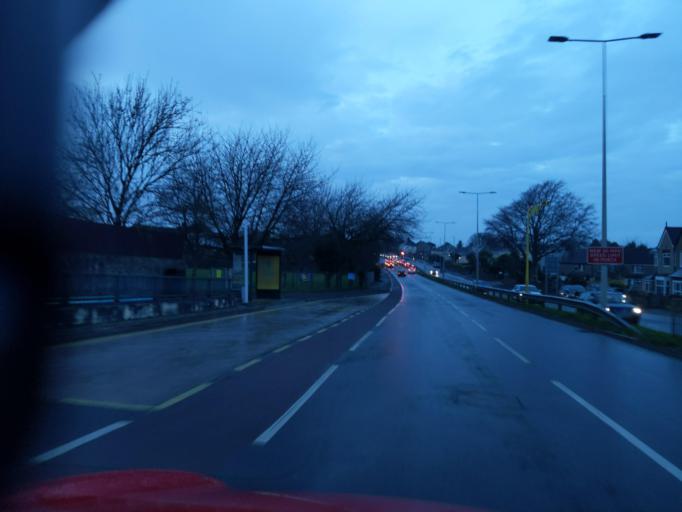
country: GB
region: England
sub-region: Plymouth
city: Plymstock
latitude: 50.3597
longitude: -4.0638
